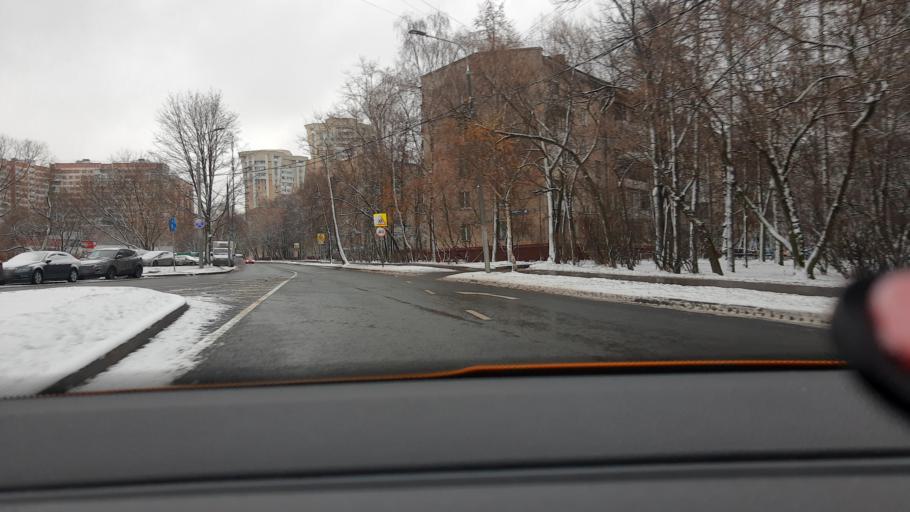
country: RU
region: Moscow
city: Strogino
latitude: 55.8447
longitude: 37.4205
